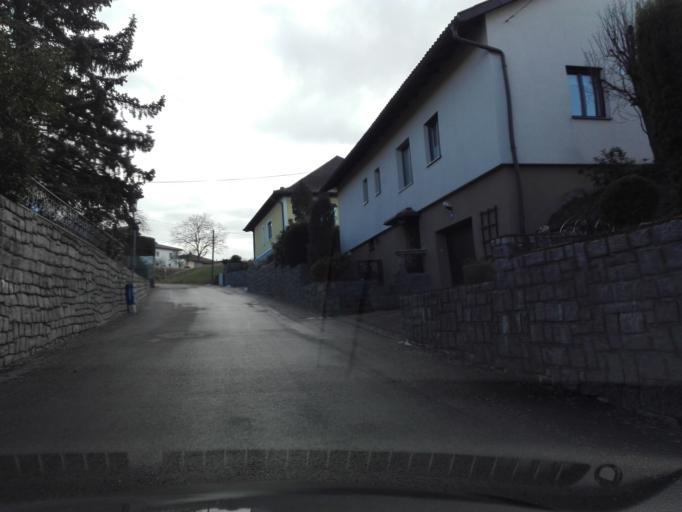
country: AT
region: Upper Austria
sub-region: Politischer Bezirk Perg
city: Perg
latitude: 48.2719
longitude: 14.5860
